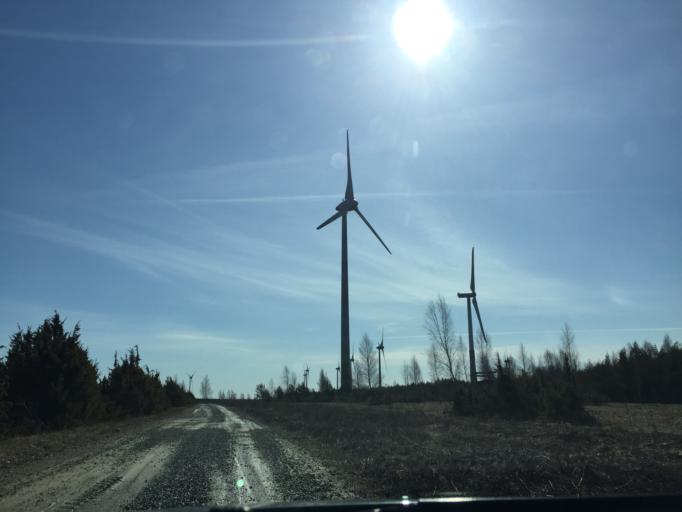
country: EE
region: Laeaene
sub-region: Haapsalu linn
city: Haapsalu
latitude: 58.6304
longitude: 23.5279
